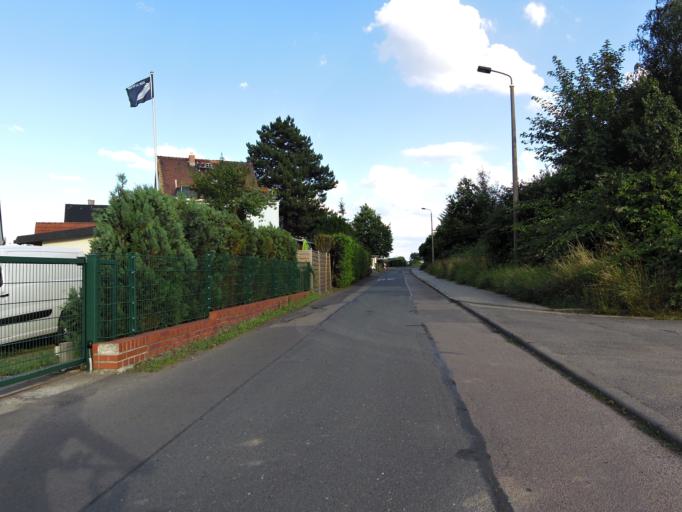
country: DE
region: Saxony
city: Taucha
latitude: 51.3292
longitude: 12.4461
